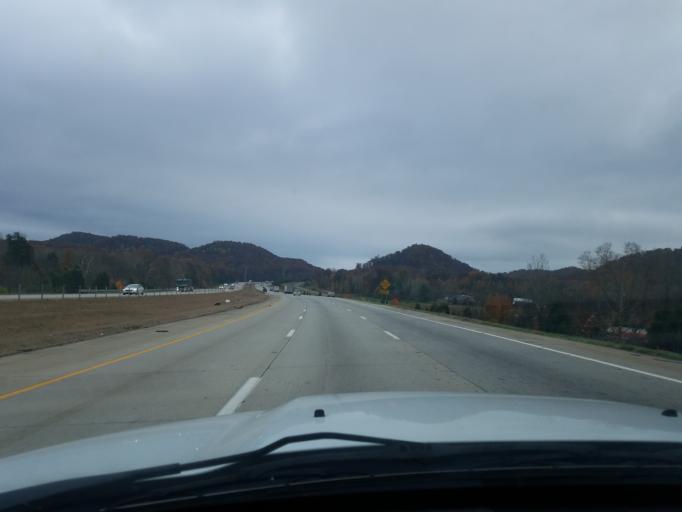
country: US
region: Kentucky
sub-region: Bullitt County
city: Lebanon Junction
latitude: 37.8943
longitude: -85.6999
